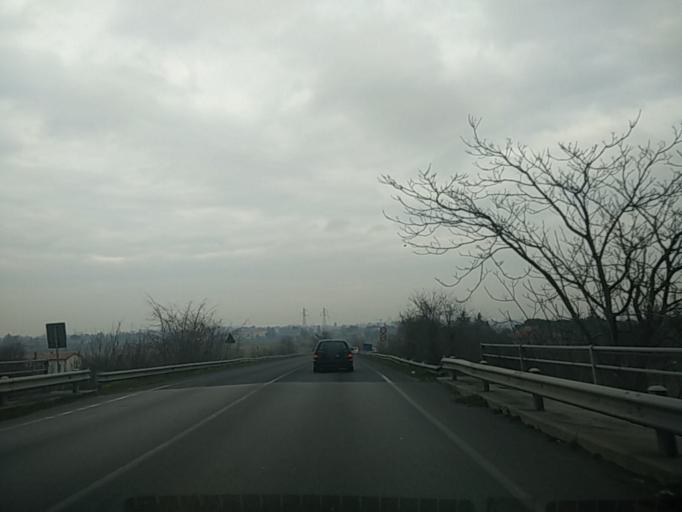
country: IT
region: Emilia-Romagna
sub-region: Provincia di Rimini
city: Santarcangelo
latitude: 44.0709
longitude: 12.4607
